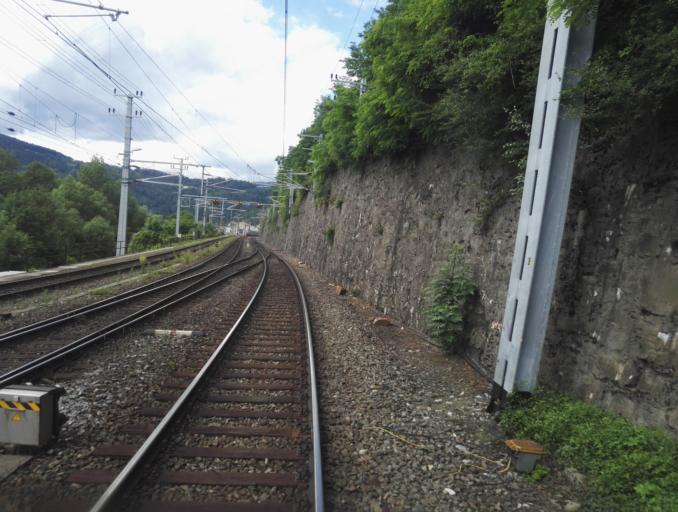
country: AT
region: Styria
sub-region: Politischer Bezirk Bruck-Muerzzuschlag
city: Bruck an der Mur
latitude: 47.4188
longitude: 15.2809
